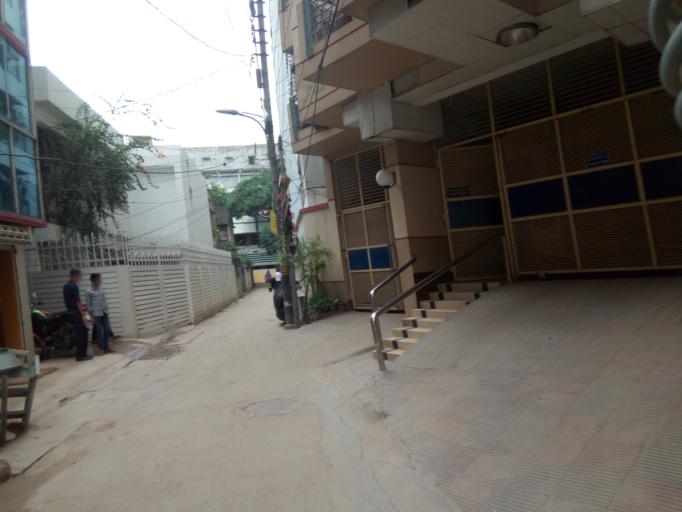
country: BD
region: Dhaka
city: Paltan
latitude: 23.7457
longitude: 90.4116
